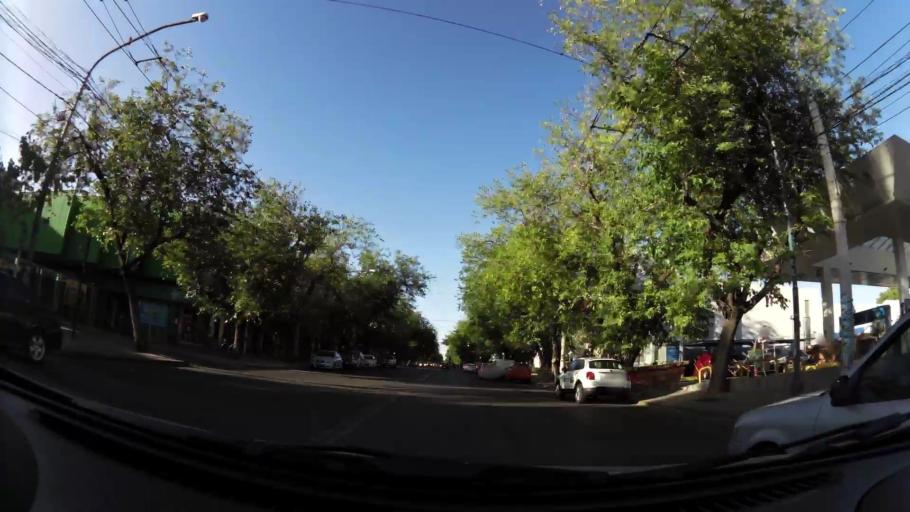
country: AR
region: Mendoza
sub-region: Departamento de Godoy Cruz
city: Godoy Cruz
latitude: -32.9174
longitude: -68.8465
